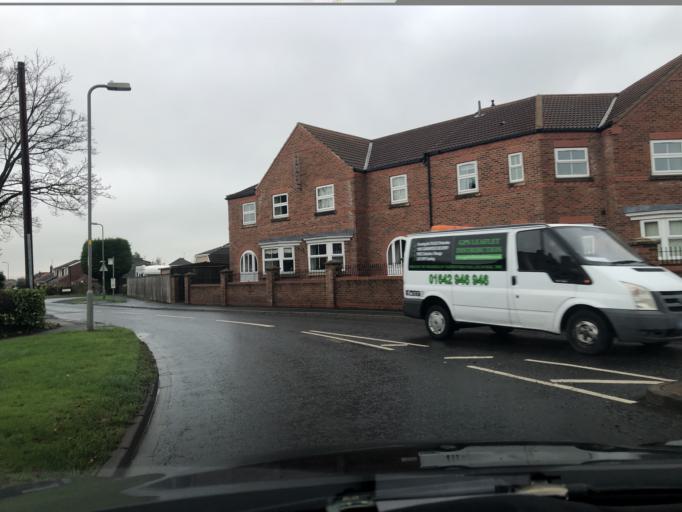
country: GB
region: England
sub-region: North Yorkshire
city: Stokesley
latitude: 54.4748
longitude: -1.1867
